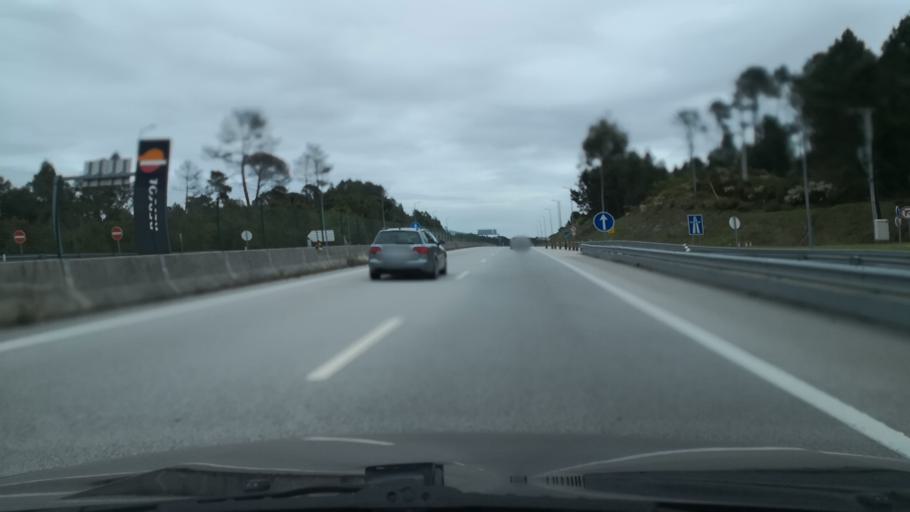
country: PT
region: Viseu
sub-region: Viseu
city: Viseu
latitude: 40.6239
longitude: -7.9315
